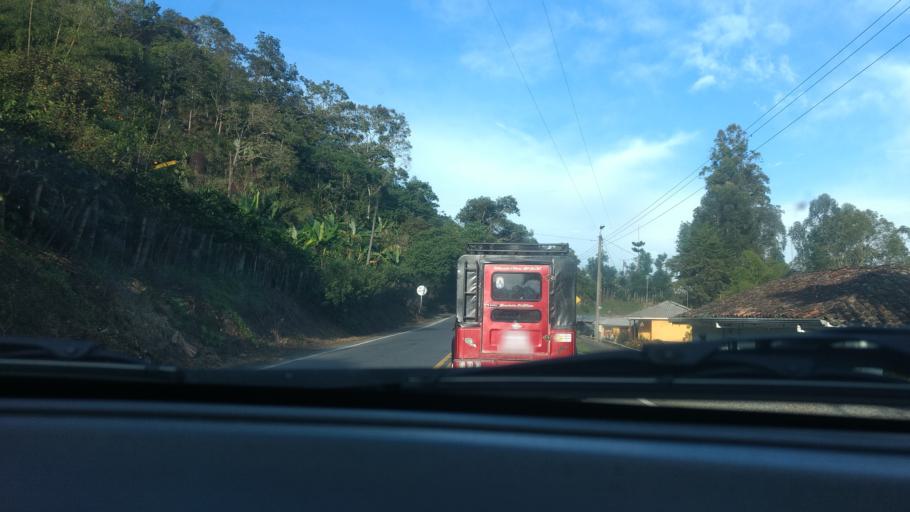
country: CO
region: Cauca
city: Rosas
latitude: 2.3063
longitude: -76.6963
